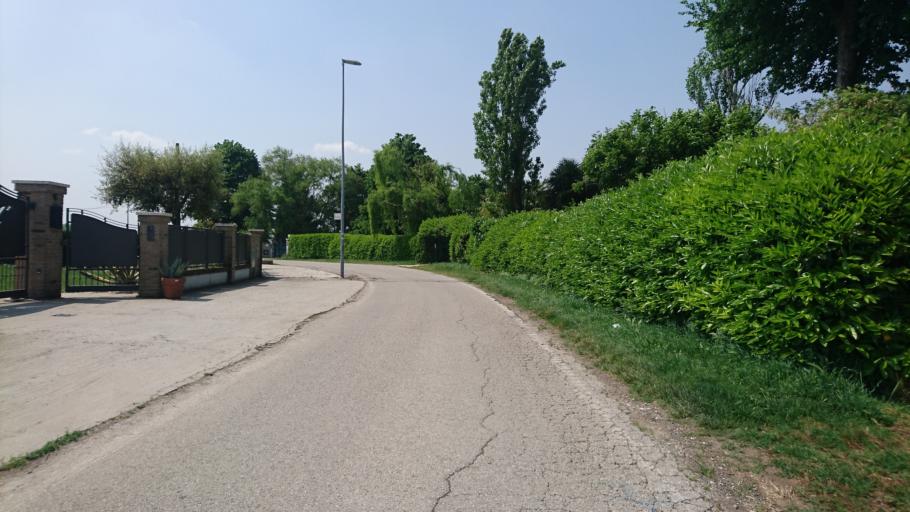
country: IT
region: Veneto
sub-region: Provincia di Venezia
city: Campagna Lupia
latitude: 45.3703
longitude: 12.1218
